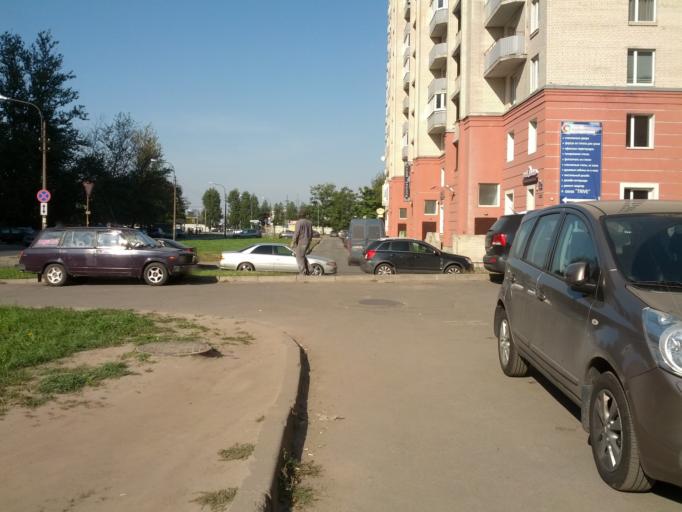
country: RU
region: St.-Petersburg
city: Kupchino
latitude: 59.8409
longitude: 30.3493
